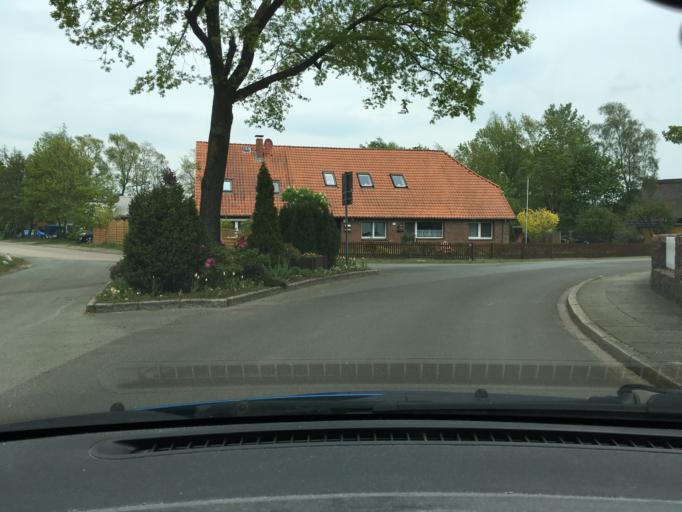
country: DE
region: Lower Saxony
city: Winsen
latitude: 53.3421
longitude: 10.1906
